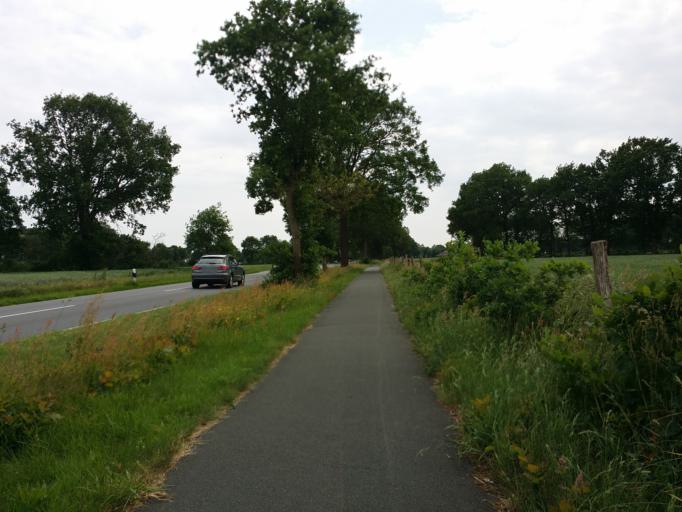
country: DE
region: Lower Saxony
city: Wiefelstede
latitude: 53.2715
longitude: 8.1109
